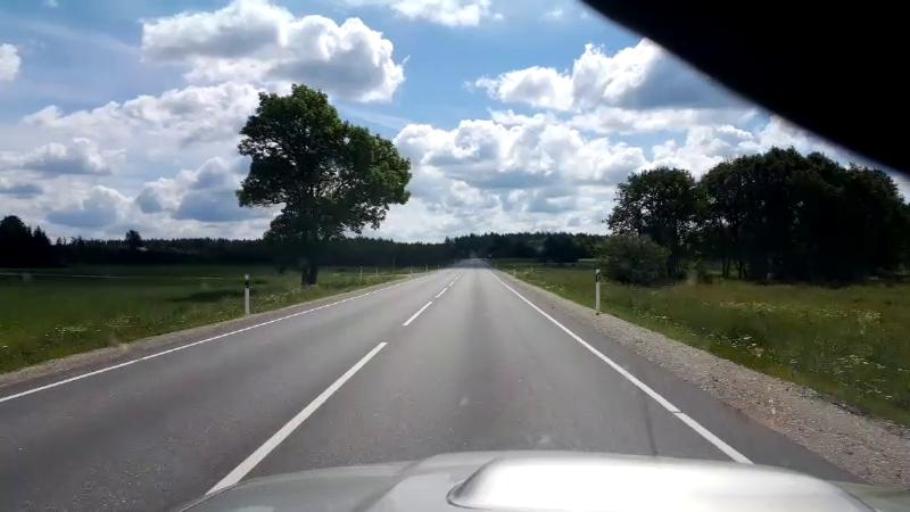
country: EE
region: Jaervamaa
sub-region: Jaerva-Jaani vald
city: Jarva-Jaani
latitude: 59.0544
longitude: 25.6993
